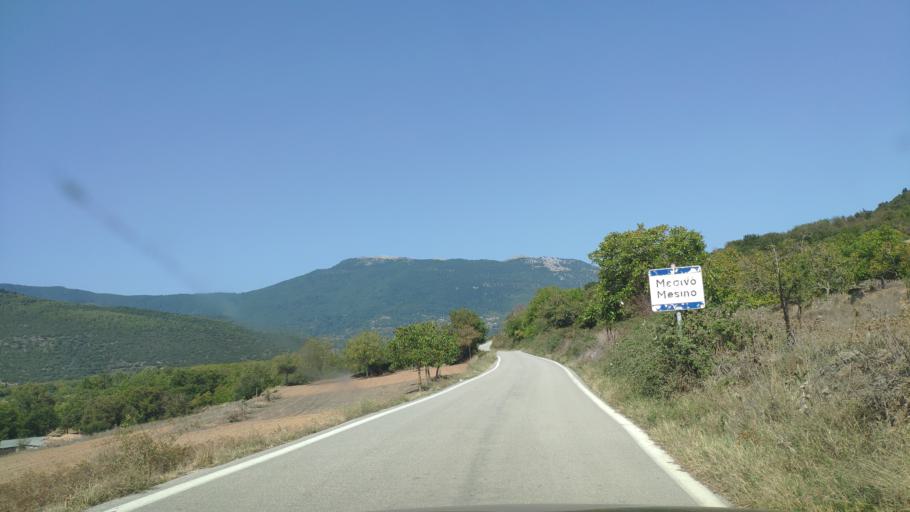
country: GR
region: West Greece
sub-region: Nomos Achaias
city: Aiyira
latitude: 37.9121
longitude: 22.3298
